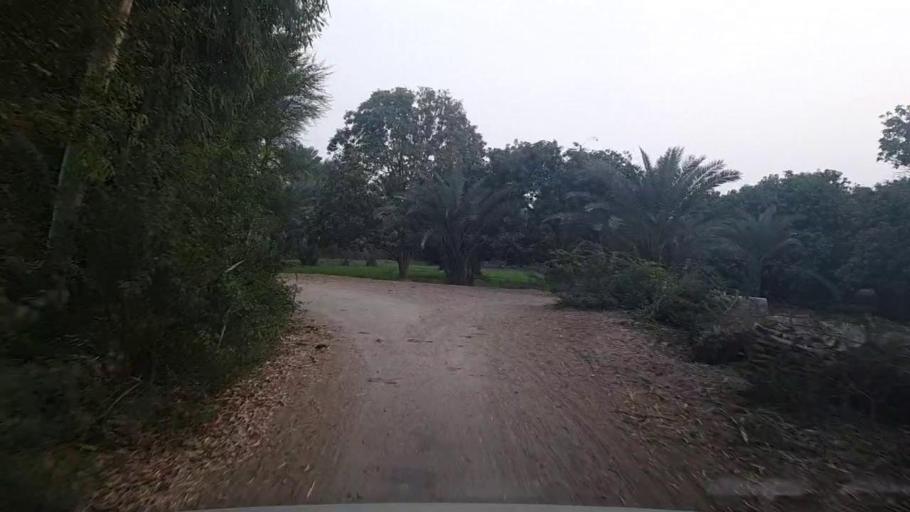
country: PK
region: Sindh
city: Kot Diji
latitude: 27.3319
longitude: 68.6400
